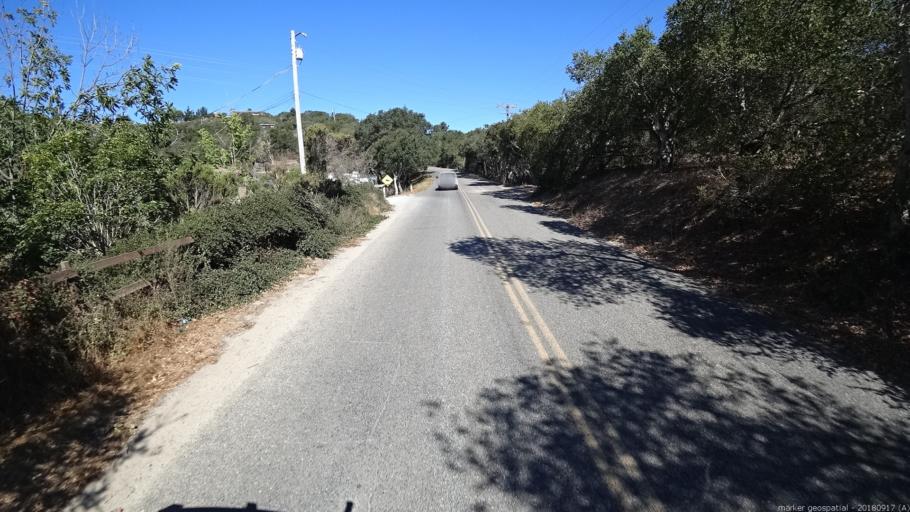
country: US
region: California
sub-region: Monterey County
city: Elkhorn
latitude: 36.8353
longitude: -121.6962
